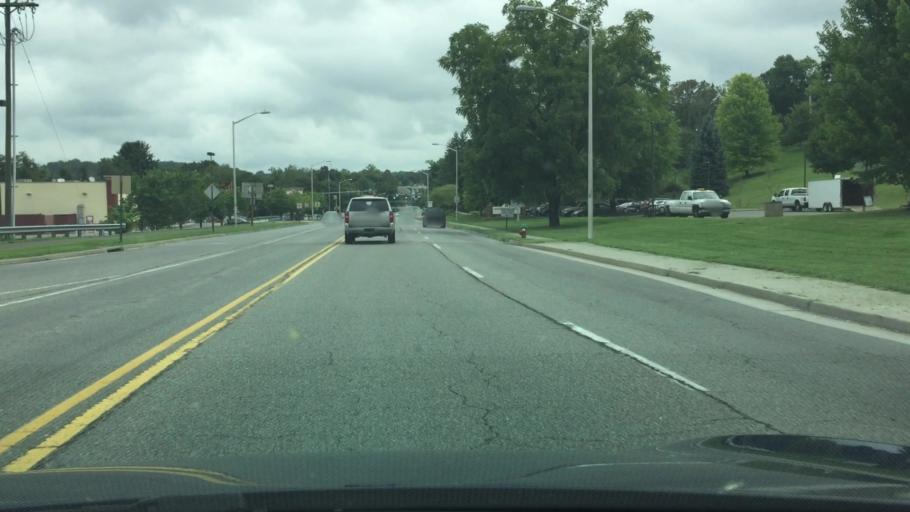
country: US
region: Virginia
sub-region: City of Radford
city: Radford
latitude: 37.1367
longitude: -80.5707
